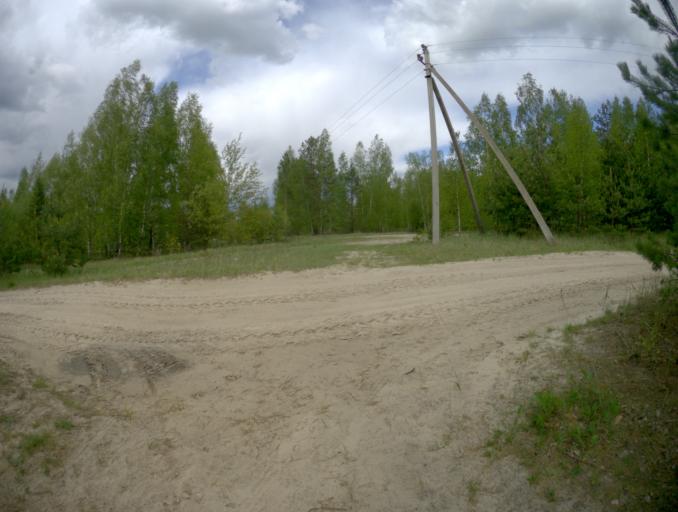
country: RU
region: Vladimir
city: Velikodvorskiy
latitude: 55.2359
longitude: 40.6524
